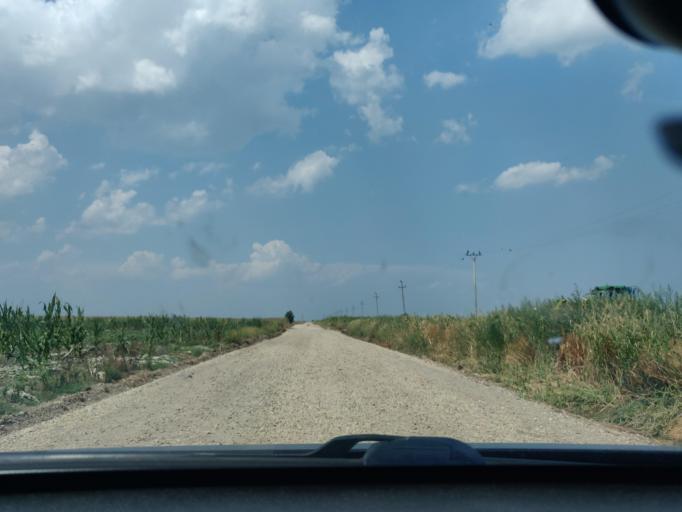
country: RO
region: Teleorman
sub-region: Comuna Sarbeni
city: Sarbeni
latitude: 44.4891
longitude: 25.3921
